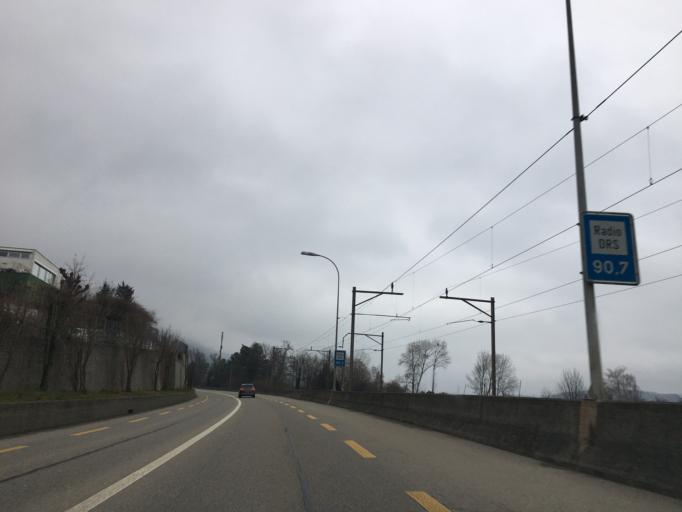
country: CH
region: Bern
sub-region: Jura bernois
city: La Neuveville
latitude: 47.0682
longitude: 7.1094
